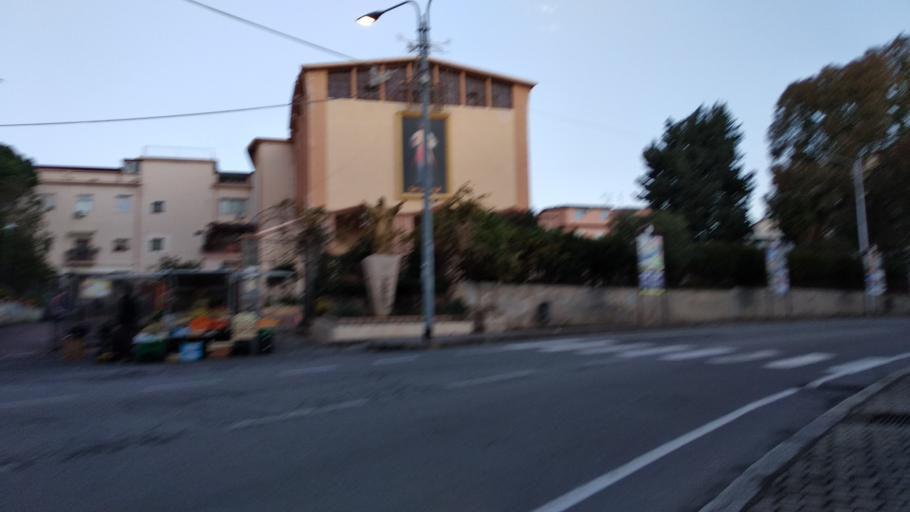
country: IT
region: Calabria
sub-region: Provincia di Catanzaro
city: Roccelletta
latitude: 38.8274
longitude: 16.6217
